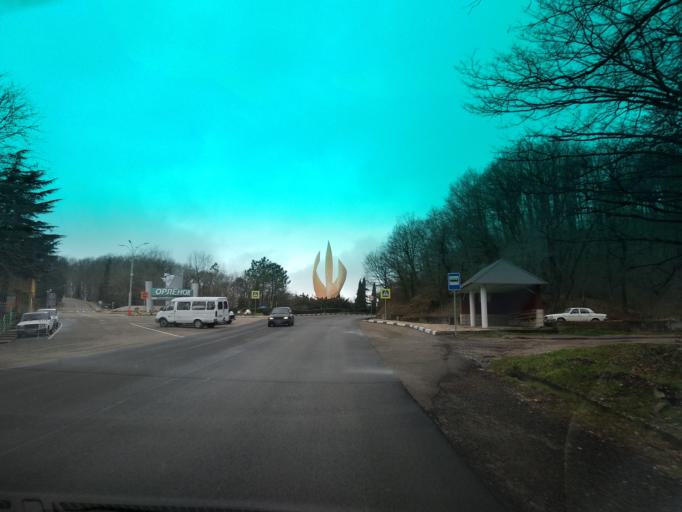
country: RU
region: Krasnodarskiy
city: Novomikhaylovskiy
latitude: 44.2550
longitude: 38.8316
